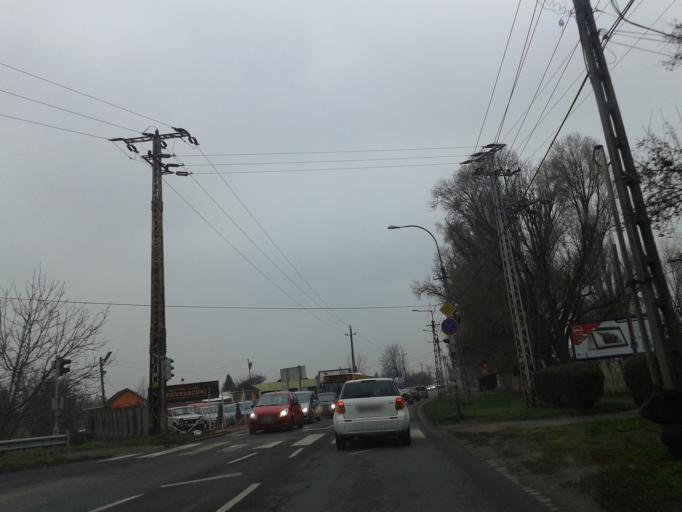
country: HU
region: Budapest
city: Budapest XXII. keruelet
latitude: 47.3985
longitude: 19.0495
